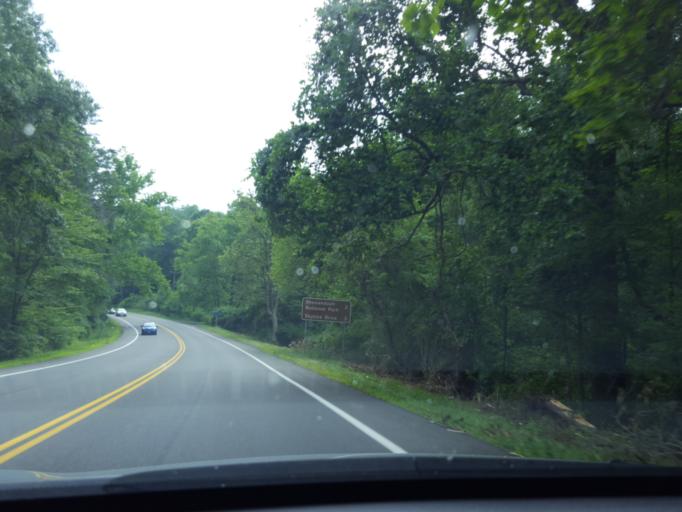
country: US
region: Virginia
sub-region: City of Waynesboro
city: Waynesboro
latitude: 38.0501
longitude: -78.8686
